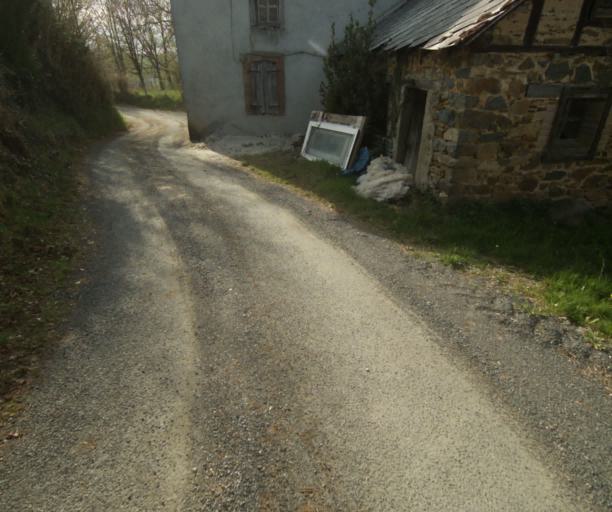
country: FR
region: Limousin
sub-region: Departement de la Correze
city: Naves
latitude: 45.3013
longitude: 1.7303
